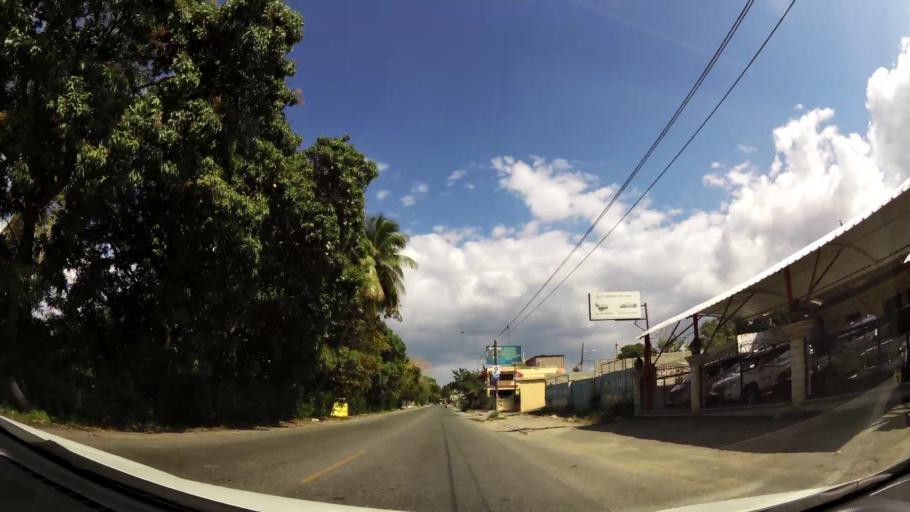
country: DO
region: San Cristobal
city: San Cristobal
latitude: 18.4258
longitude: -70.0734
